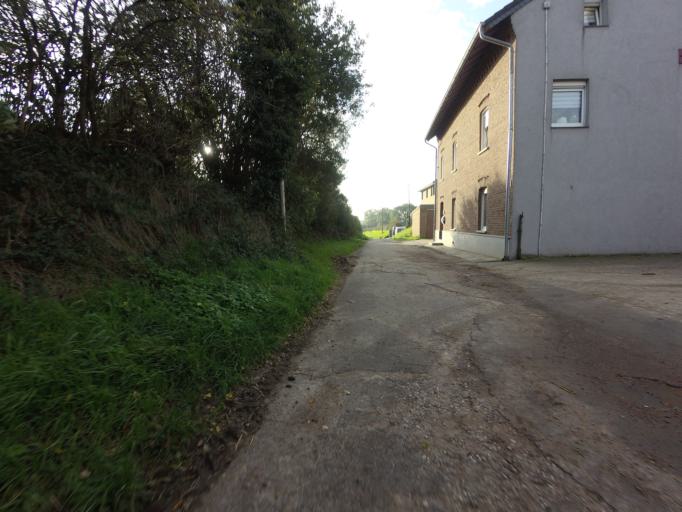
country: DE
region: North Rhine-Westphalia
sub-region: Regierungsbezirk Koln
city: Herzogenrath
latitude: 50.8866
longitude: 6.0967
